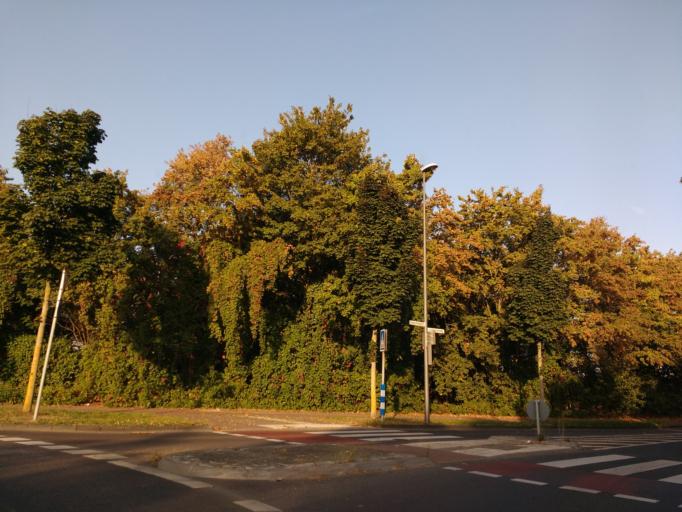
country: DE
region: North Rhine-Westphalia
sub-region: Regierungsbezirk Koln
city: Bilderstoeckchen
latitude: 50.9923
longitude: 6.9029
